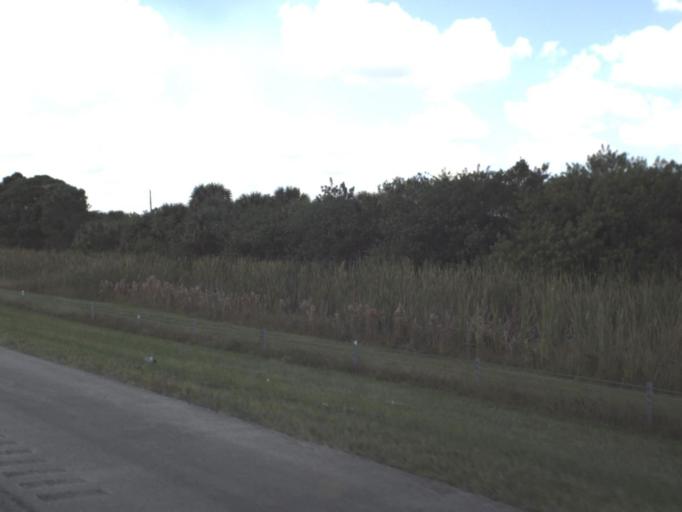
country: US
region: Florida
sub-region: Saint Lucie County
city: Lakewood Park
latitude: 27.4848
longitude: -80.4895
